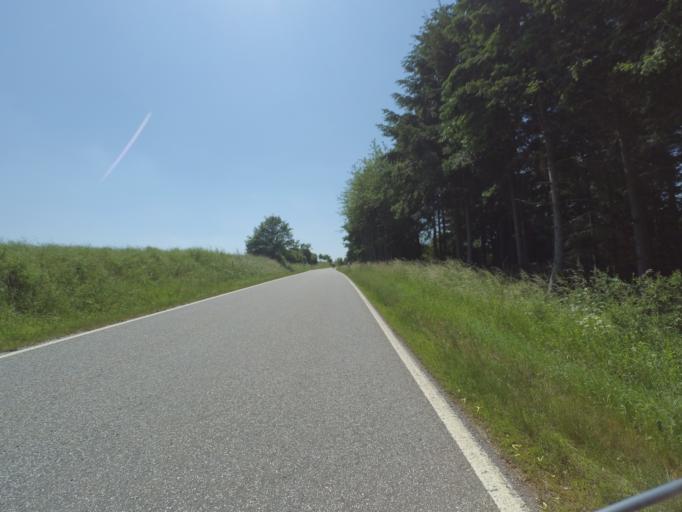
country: DE
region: Rheinland-Pfalz
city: Morsdorf
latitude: 50.1091
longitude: 7.3584
